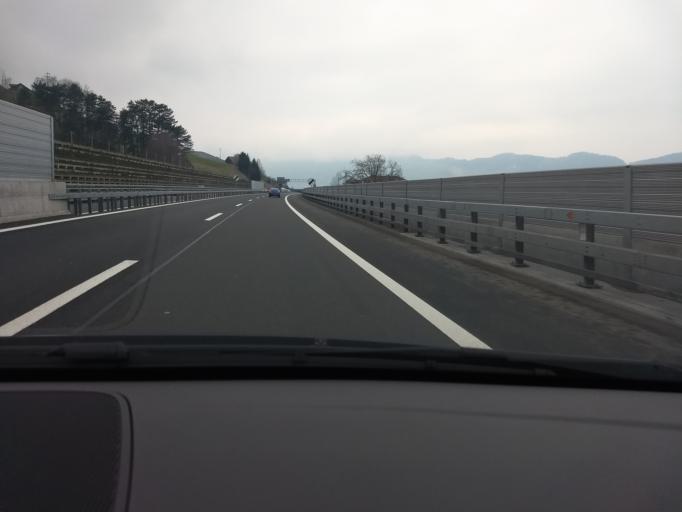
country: CH
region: Nidwalden
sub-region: Nidwalden
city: Beckenried
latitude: 46.9639
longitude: 8.4684
